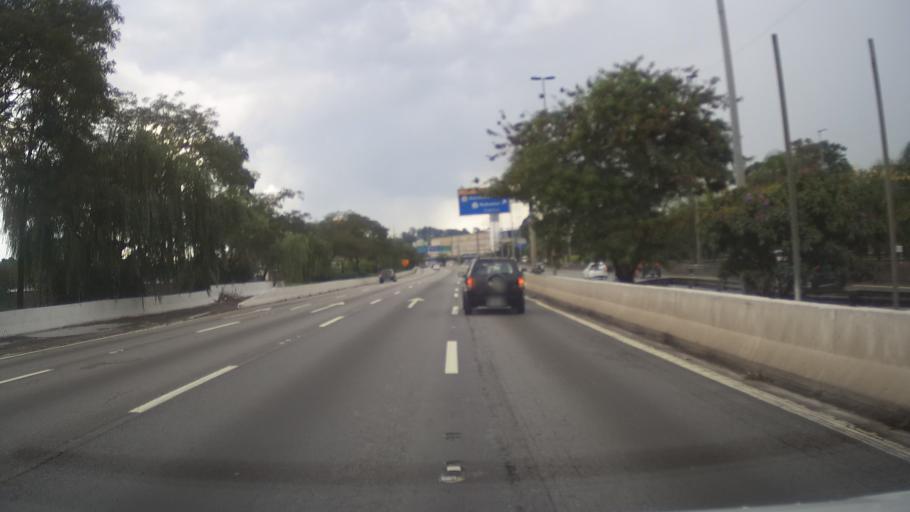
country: BR
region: Sao Paulo
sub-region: Sao Paulo
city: Sao Paulo
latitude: -23.5069
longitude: -46.7098
